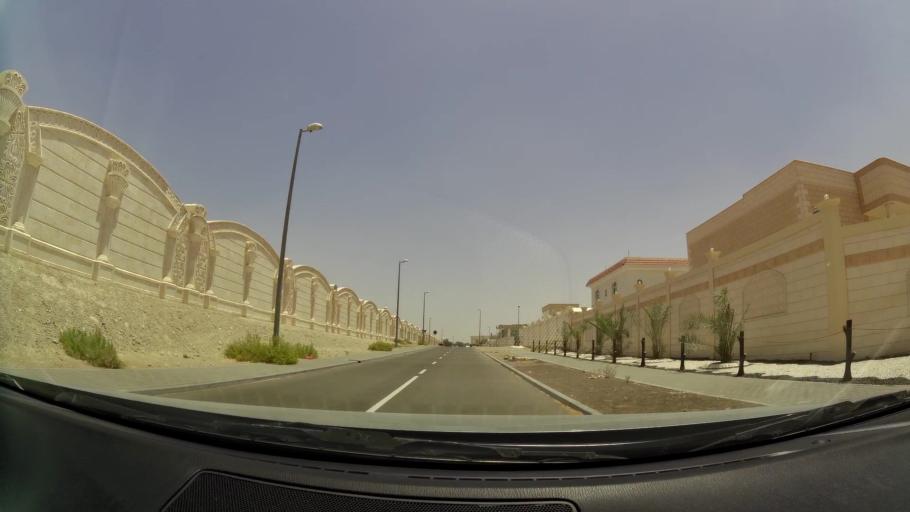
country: OM
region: Al Buraimi
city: Al Buraymi
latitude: 24.2713
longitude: 55.7152
